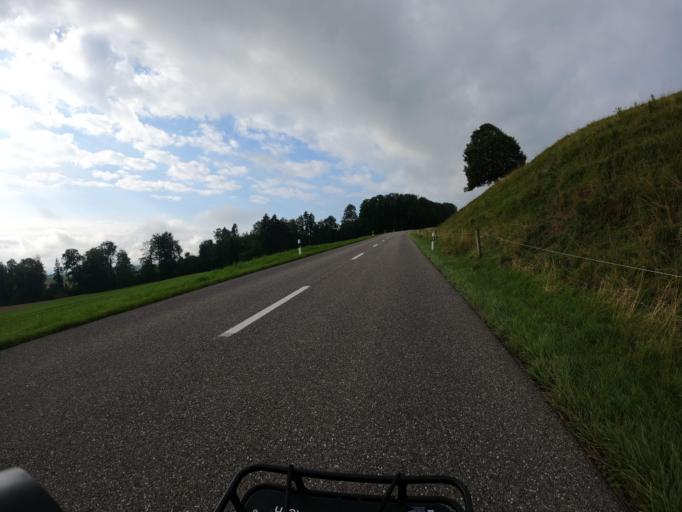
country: CH
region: Aargau
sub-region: Bezirk Muri
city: Buttwil
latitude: 47.2606
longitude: 8.3224
